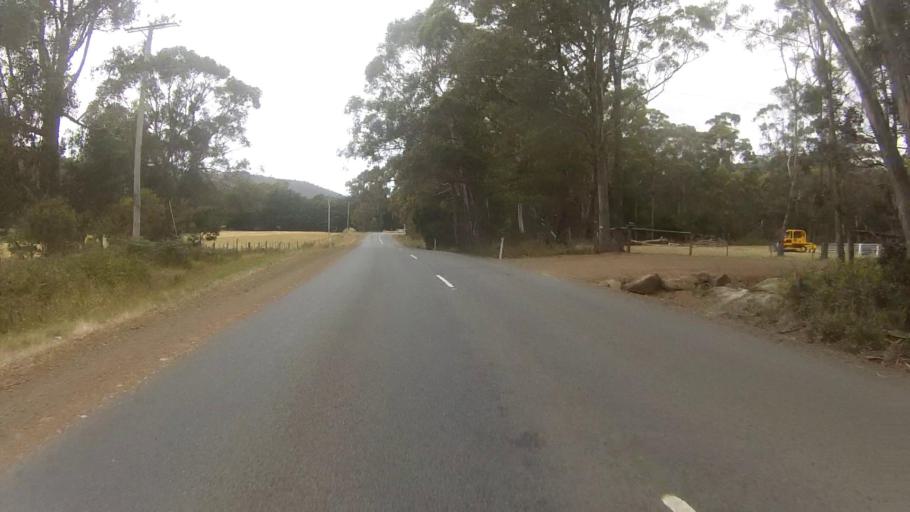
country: AU
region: Tasmania
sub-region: Kingborough
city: Margate
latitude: -42.9933
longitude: 147.2180
